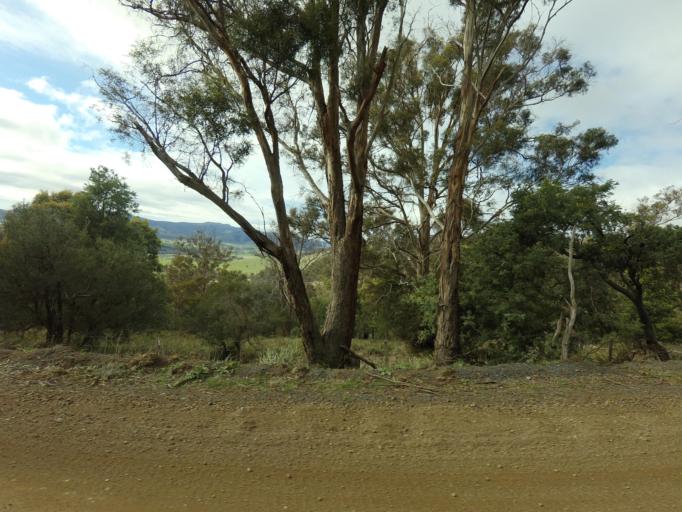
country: AU
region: Tasmania
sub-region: Derwent Valley
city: New Norfolk
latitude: -42.7282
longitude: 146.8664
